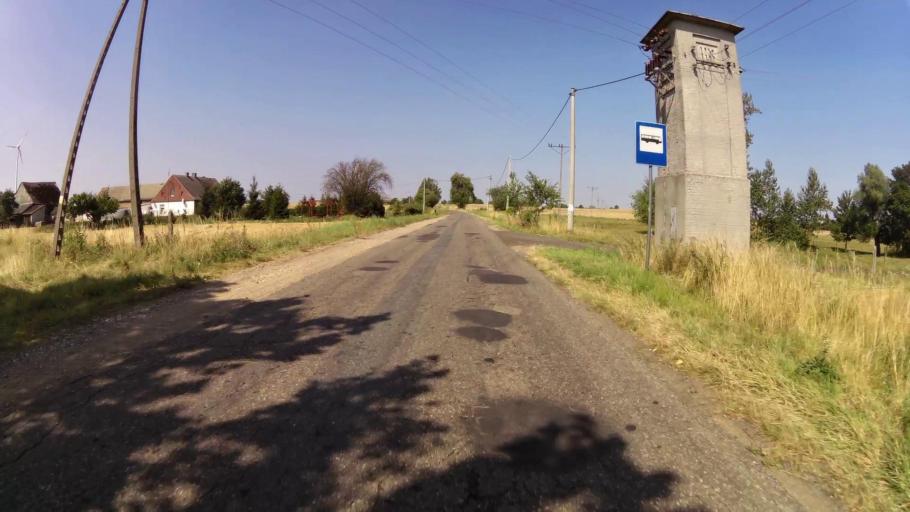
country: PL
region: West Pomeranian Voivodeship
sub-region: Powiat walecki
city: Walcz
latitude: 53.2201
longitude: 16.4714
